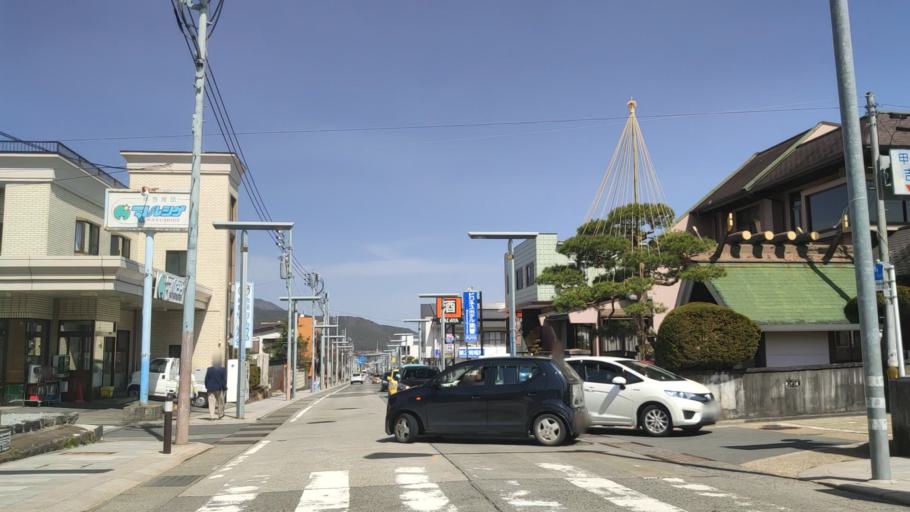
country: JP
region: Yamanashi
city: Fujikawaguchiko
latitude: 35.4807
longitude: 138.7961
